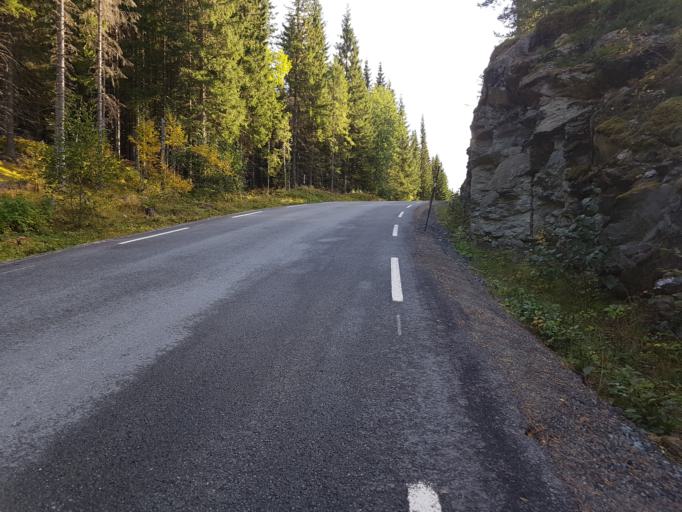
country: NO
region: Sor-Trondelag
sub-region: Malvik
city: Malvik
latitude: 63.3531
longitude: 10.6405
